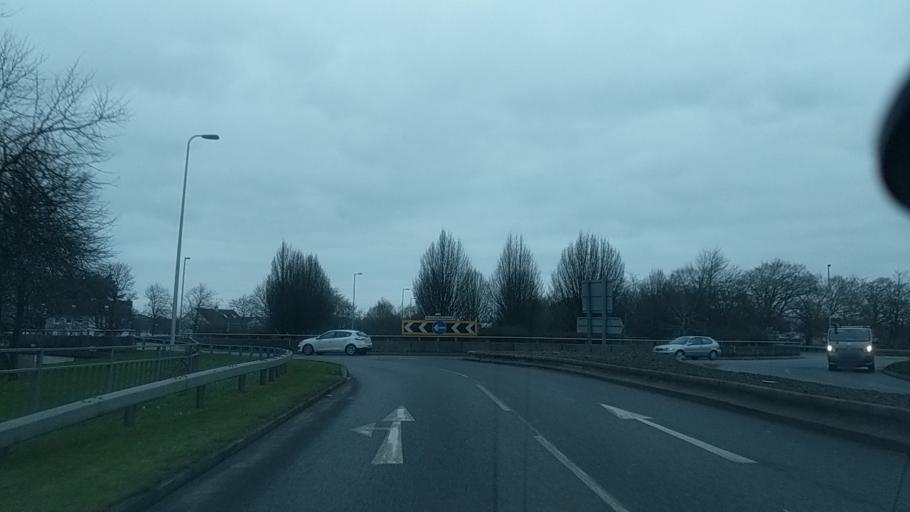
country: GB
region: Scotland
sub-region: South Lanarkshire
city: East Kilbride
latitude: 55.7626
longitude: -4.1654
